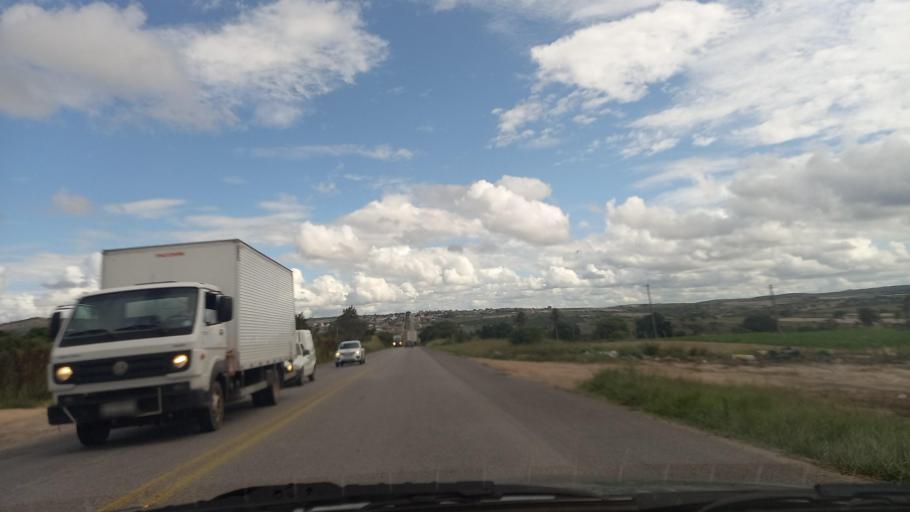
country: BR
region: Pernambuco
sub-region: Lajedo
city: Lajedo
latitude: -8.6870
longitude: -36.4092
